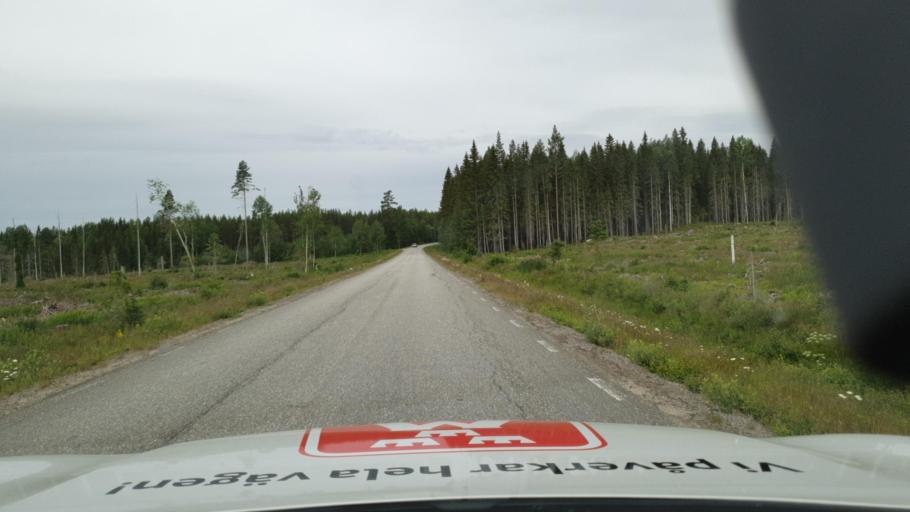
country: SE
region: Vaesterbotten
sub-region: Robertsfors Kommun
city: Robertsfors
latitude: 64.2873
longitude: 20.6518
